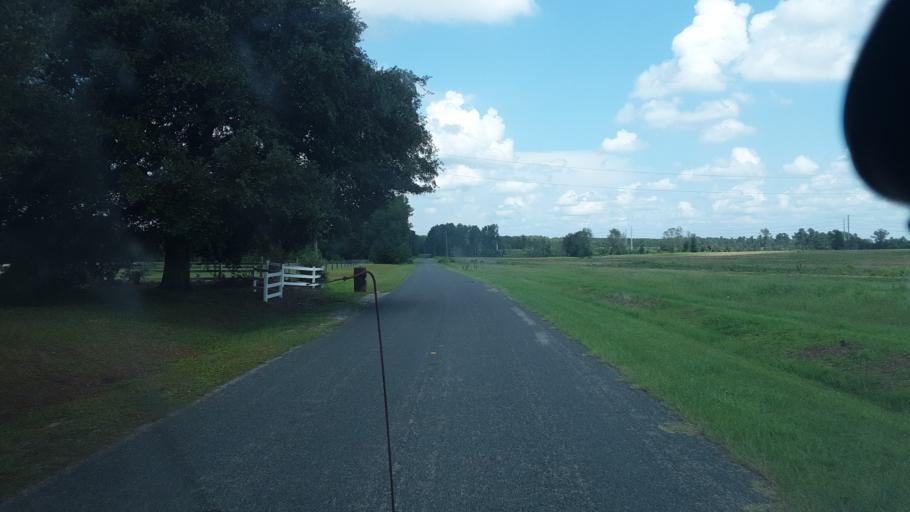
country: US
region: South Carolina
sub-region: Calhoun County
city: Oak Grove
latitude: 33.6742
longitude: -80.9710
